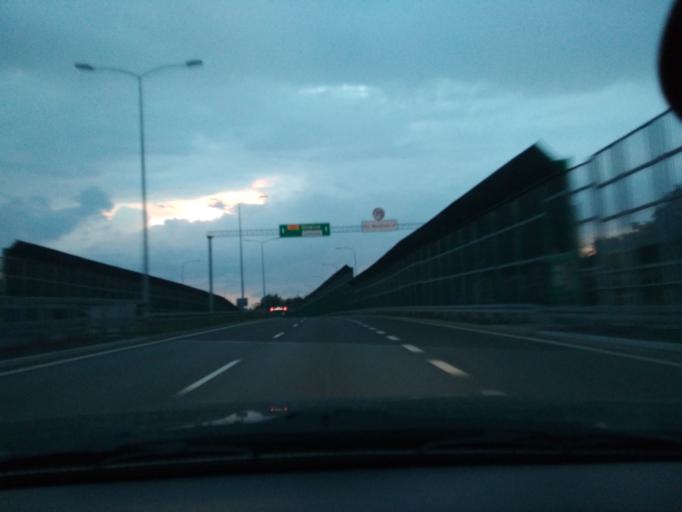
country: PL
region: Silesian Voivodeship
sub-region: Gliwice
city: Gliwice
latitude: 50.2893
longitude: 18.7012
